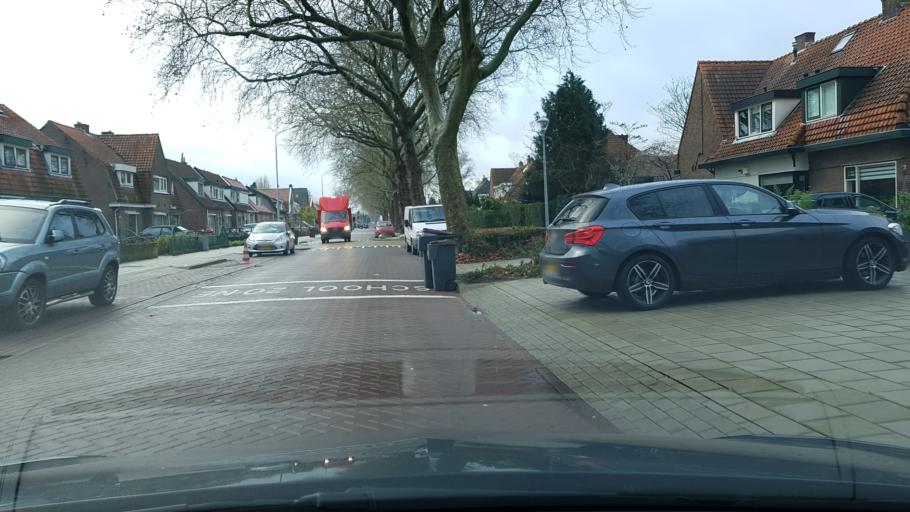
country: NL
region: North Holland
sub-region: Gemeente Zaanstad
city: Zaandam
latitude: 52.3760
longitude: 4.7539
